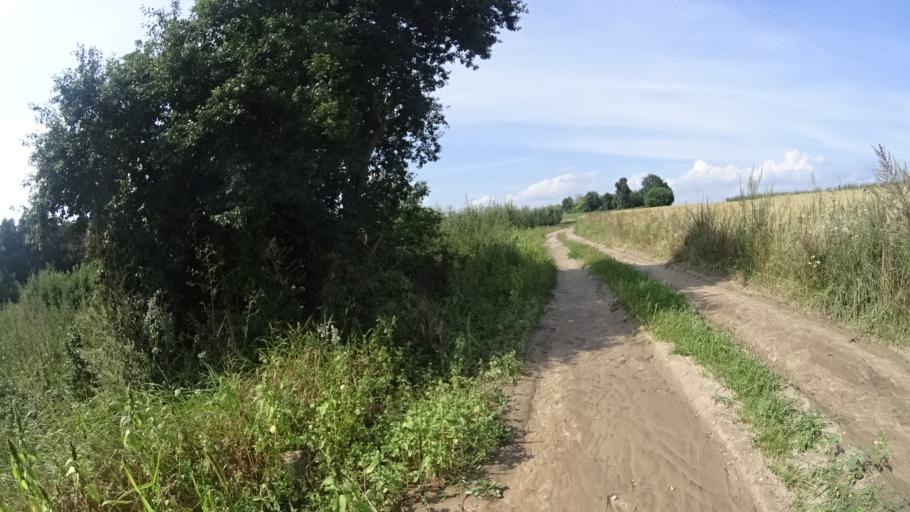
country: PL
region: Masovian Voivodeship
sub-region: Powiat grojecki
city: Goszczyn
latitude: 51.6890
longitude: 20.8396
